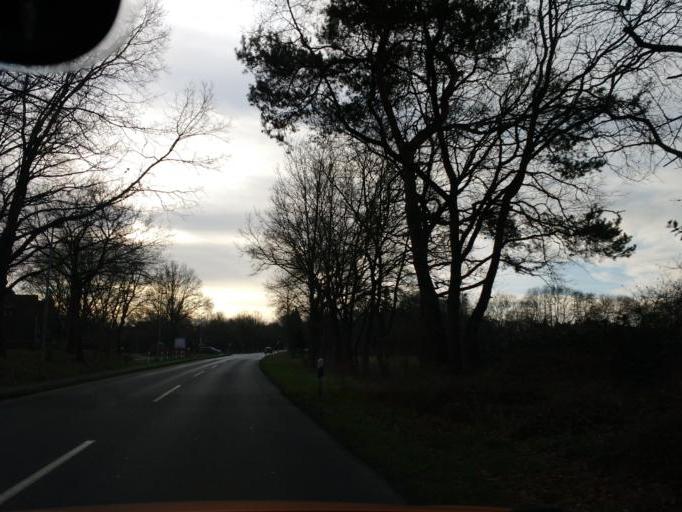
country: DE
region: Lower Saxony
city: Hude
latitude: 53.0984
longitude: 8.4547
